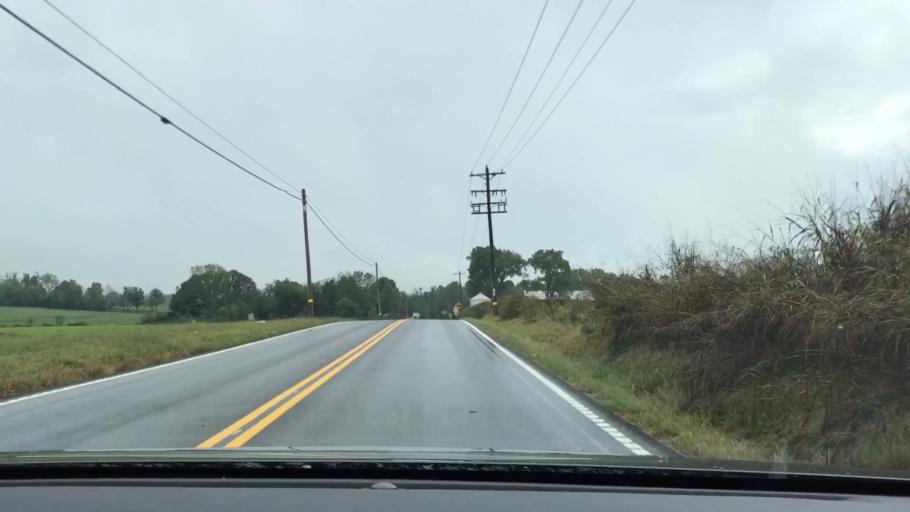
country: US
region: Tennessee
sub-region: Macon County
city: Red Boiling Springs
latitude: 36.4524
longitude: -85.8808
